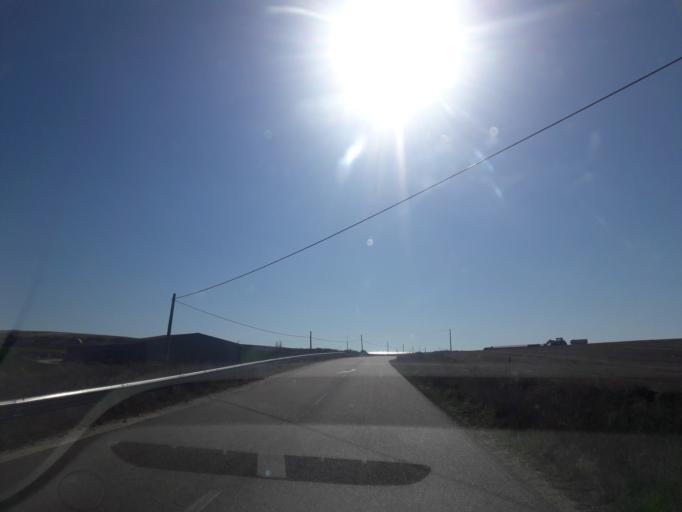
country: ES
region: Castille and Leon
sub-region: Provincia de Salamanca
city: Tordillos
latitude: 40.8532
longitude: -5.3441
